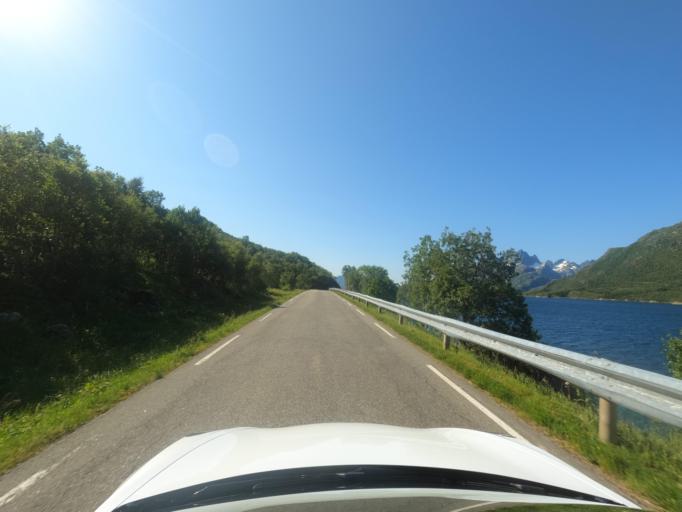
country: NO
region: Nordland
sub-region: Hadsel
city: Stokmarknes
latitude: 68.3782
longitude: 15.0838
